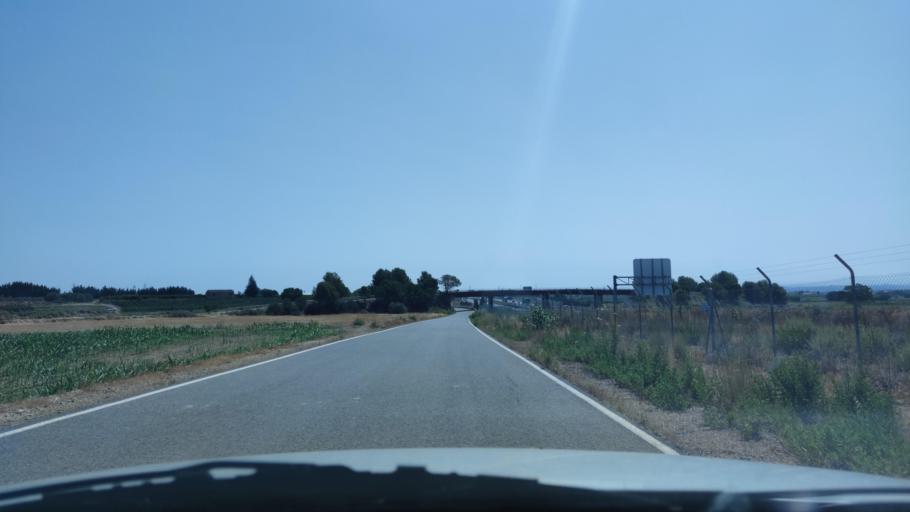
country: ES
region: Catalonia
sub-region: Provincia de Lleida
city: Torrefarrera
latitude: 41.6613
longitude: 0.5931
